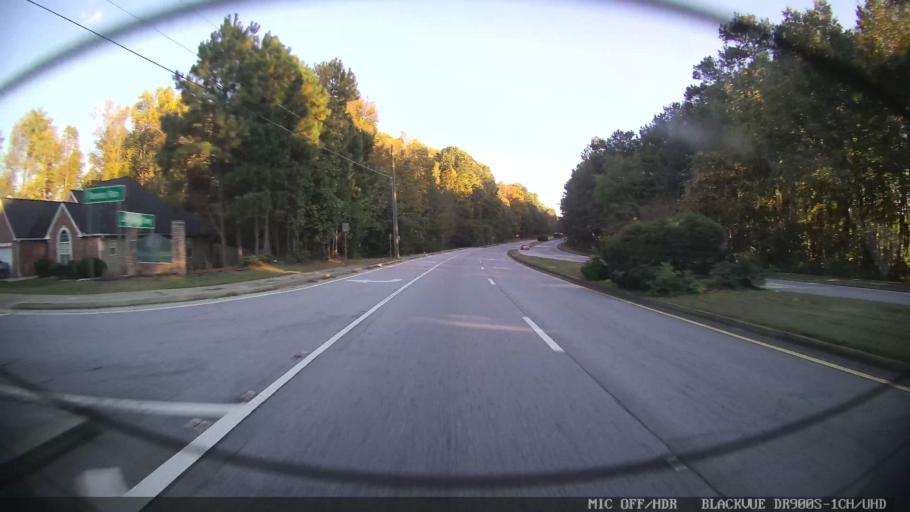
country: US
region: Georgia
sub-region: Clayton County
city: Jonesboro
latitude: 33.5377
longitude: -84.3430
